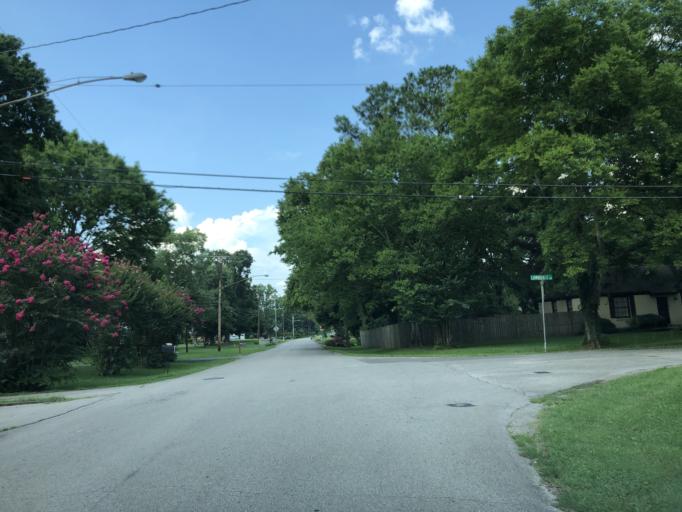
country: US
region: Tennessee
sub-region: Davidson County
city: Oak Hill
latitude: 36.1236
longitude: -86.7210
